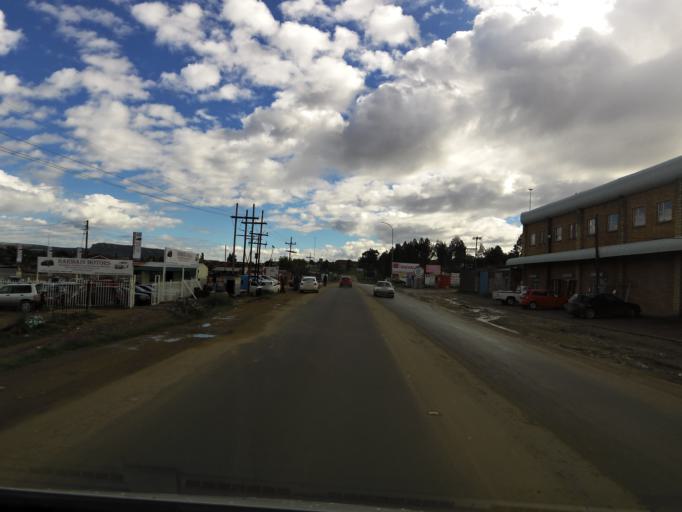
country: LS
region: Maseru
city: Maseru
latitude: -29.3019
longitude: 27.5166
